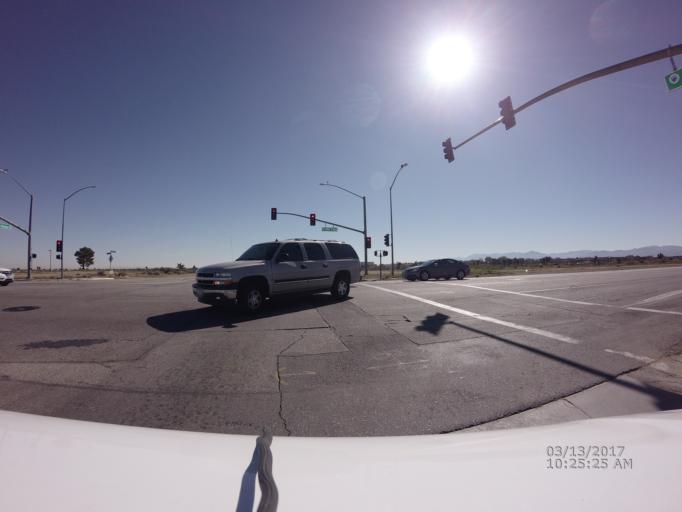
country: US
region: California
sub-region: Los Angeles County
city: Desert View Highlands
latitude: 34.6166
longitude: -118.1479
